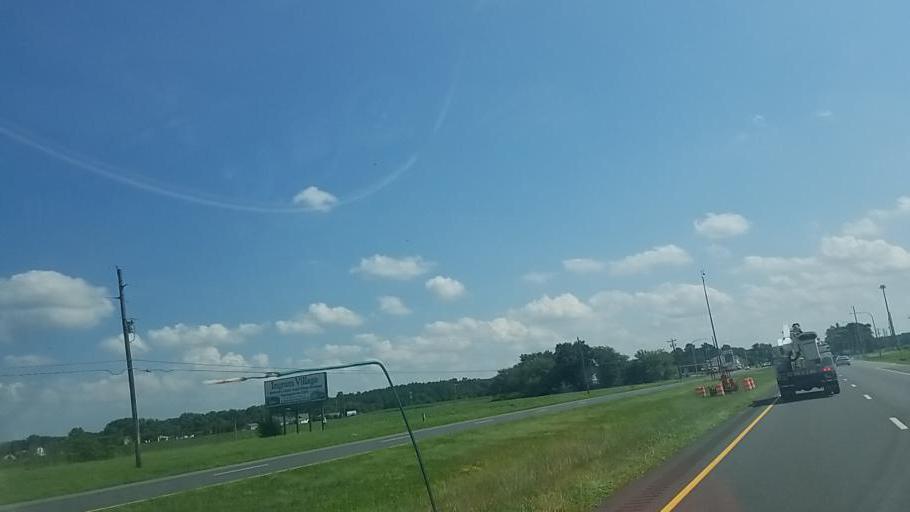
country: US
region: Delaware
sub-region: Sussex County
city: Milford
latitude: 38.8100
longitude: -75.4389
